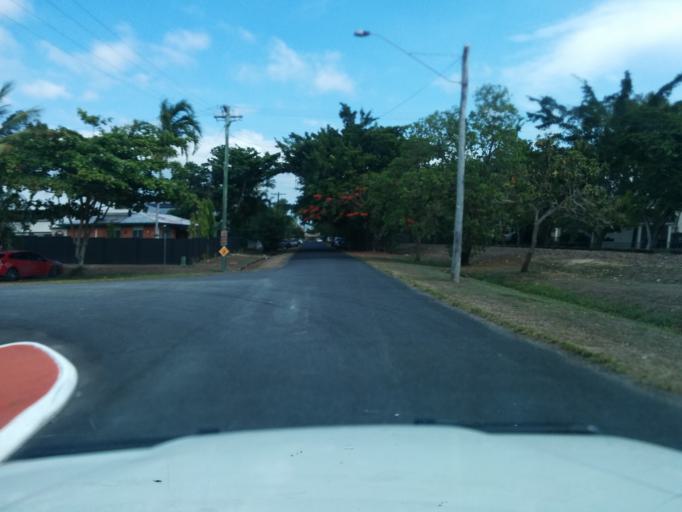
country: AU
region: Queensland
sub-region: Cairns
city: Cairns
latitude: -16.9115
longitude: 145.7601
